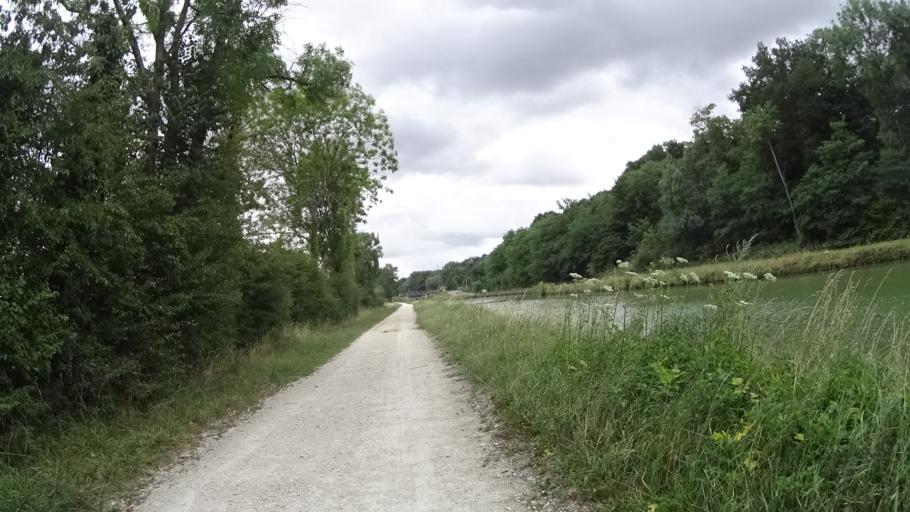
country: FR
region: Centre
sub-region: Departement du Loiret
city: Amilly
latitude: 47.9657
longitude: 2.7645
